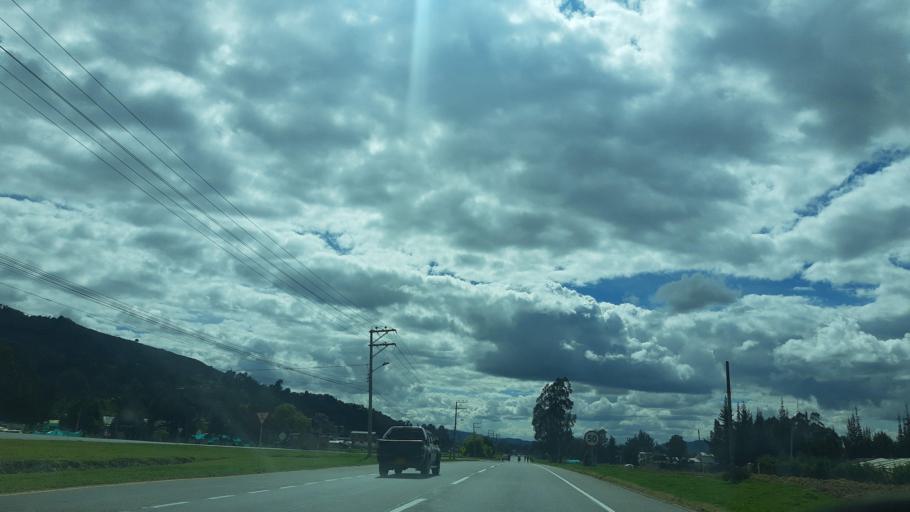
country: CO
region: Cundinamarca
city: Gachancipa
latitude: 4.9838
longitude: -73.8823
